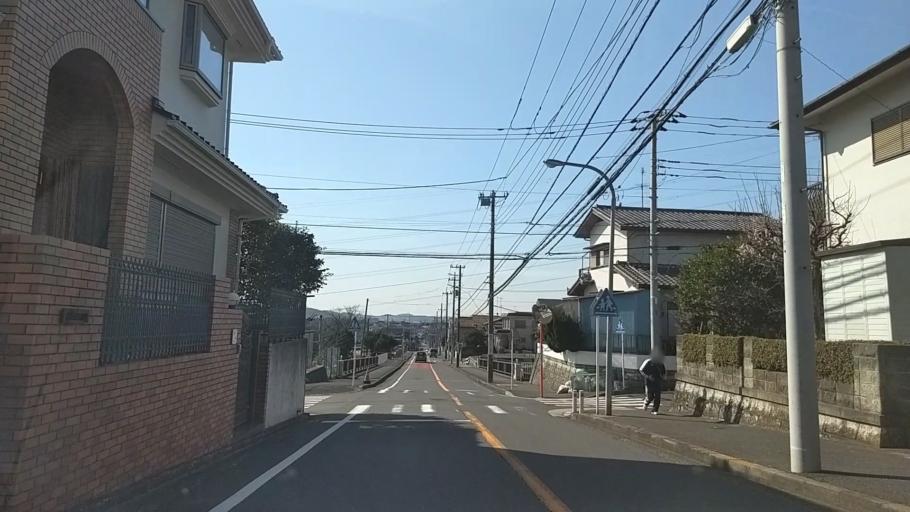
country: JP
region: Kanagawa
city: Kamakura
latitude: 35.3797
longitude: 139.5505
